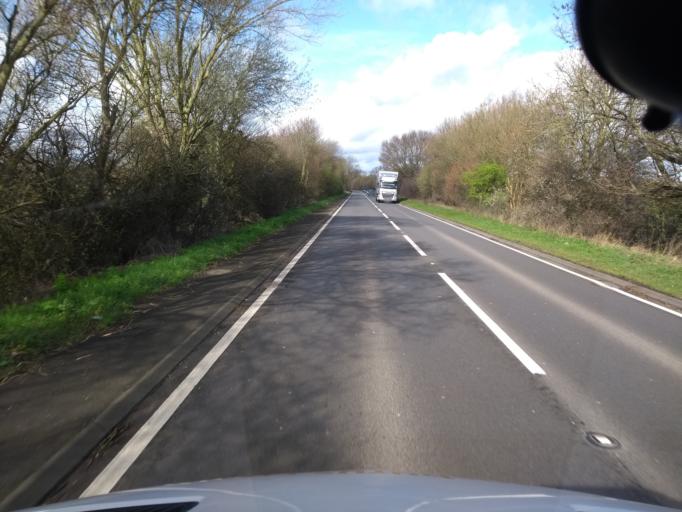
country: GB
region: England
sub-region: Somerset
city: Stoke-sub-Hamdon
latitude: 50.9634
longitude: -2.7305
